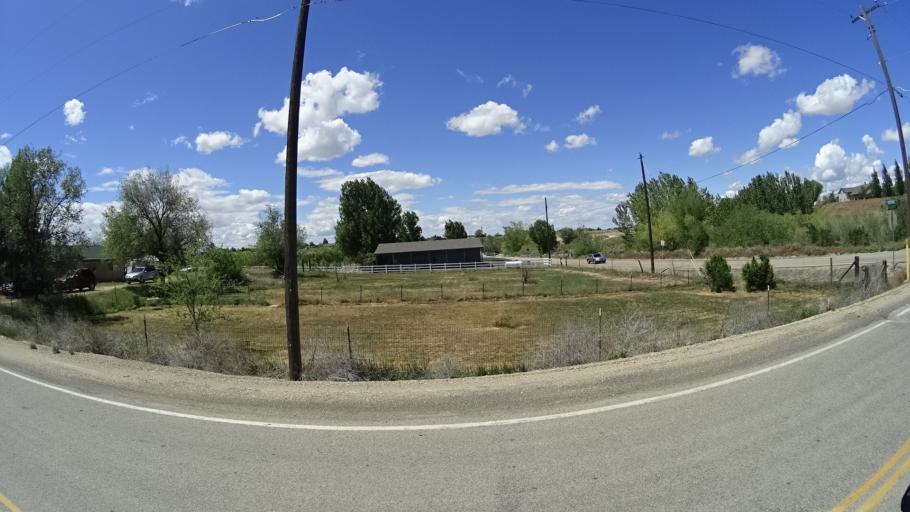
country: US
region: Idaho
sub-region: Ada County
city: Meridian
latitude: 43.5864
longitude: -116.4735
